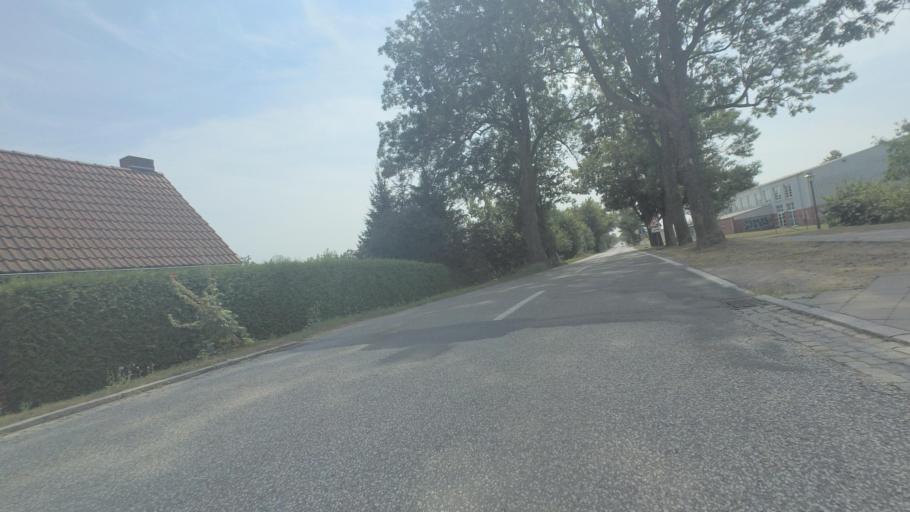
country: DE
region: Mecklenburg-Vorpommern
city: Garz
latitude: 54.3147
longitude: 13.3534
